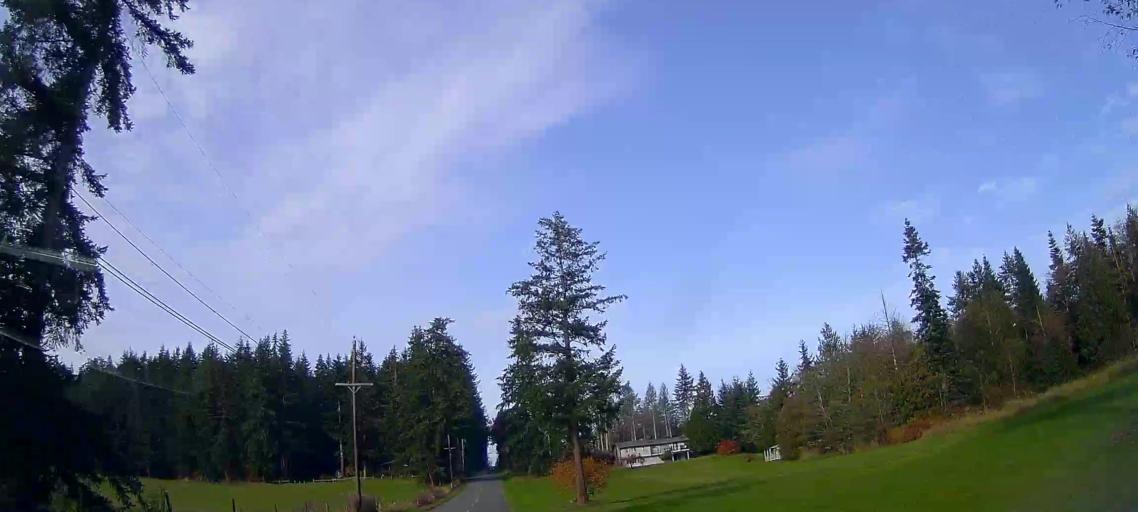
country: US
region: Washington
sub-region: Snohomish County
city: Stanwood
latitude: 48.2596
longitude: -122.3414
